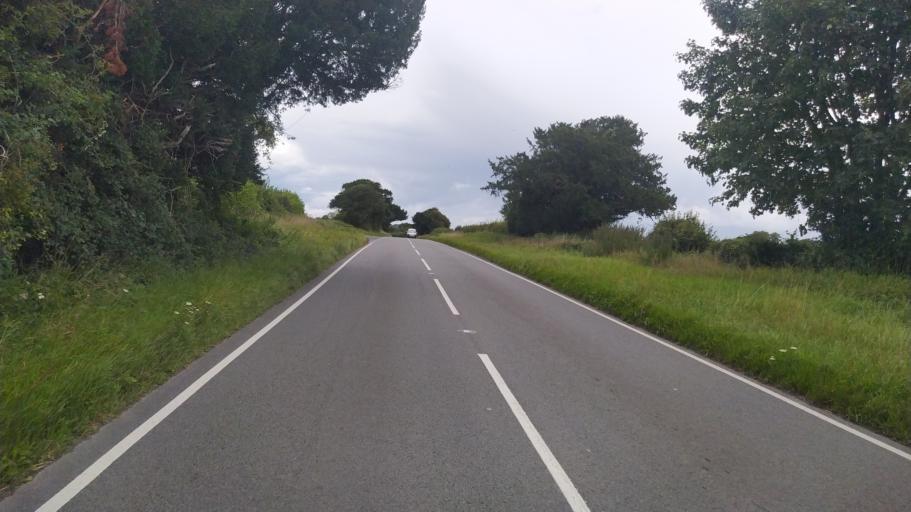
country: GB
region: England
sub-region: Dorset
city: Verwood
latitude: 50.9100
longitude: -1.9321
